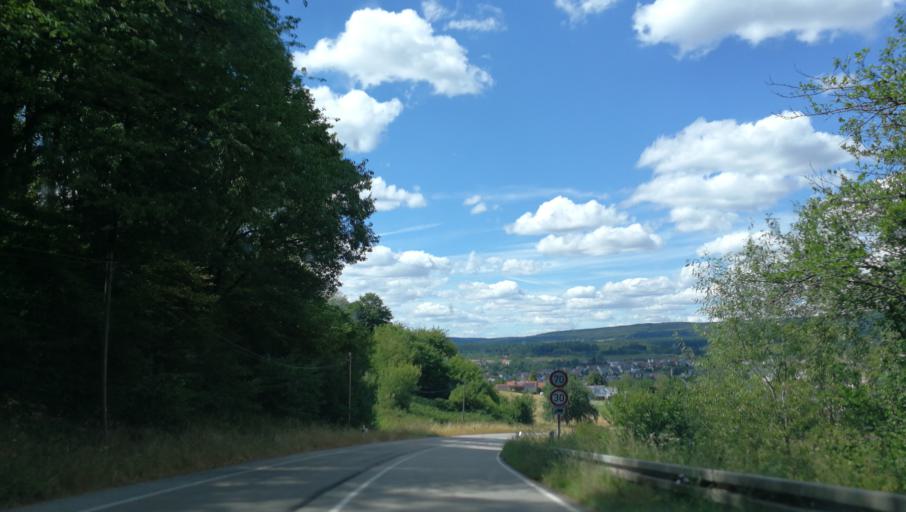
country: DE
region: Saarland
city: Losheim
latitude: 49.5005
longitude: 6.7465
